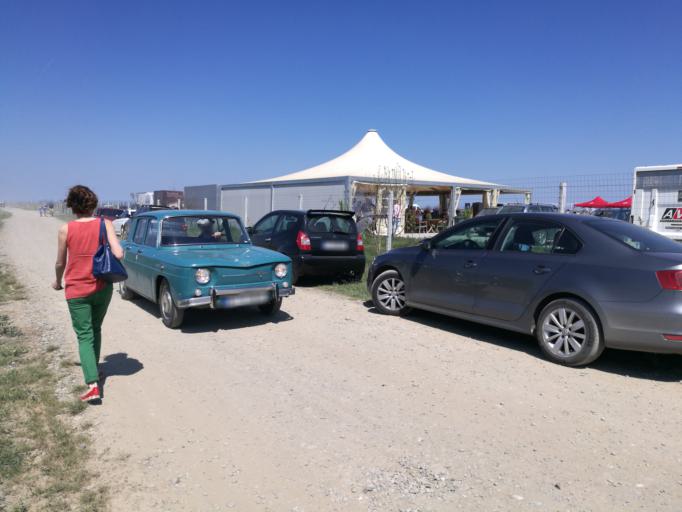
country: RO
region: Prahova
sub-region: Comuna Salciile
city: Salciile
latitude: 44.7786
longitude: 26.4721
